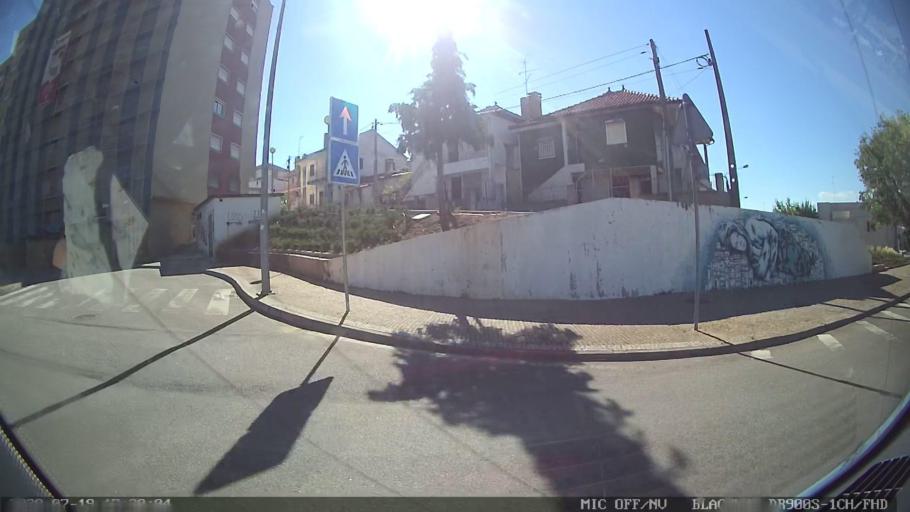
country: PT
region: Braganca
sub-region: Braganca Municipality
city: Braganca
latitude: 41.7951
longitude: -6.7707
